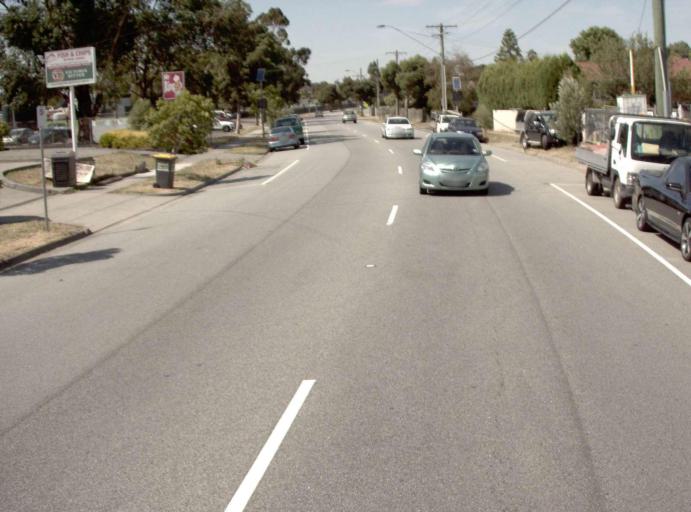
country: AU
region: Victoria
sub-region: Greater Dandenong
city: Noble Park North
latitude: -37.9464
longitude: 145.1916
